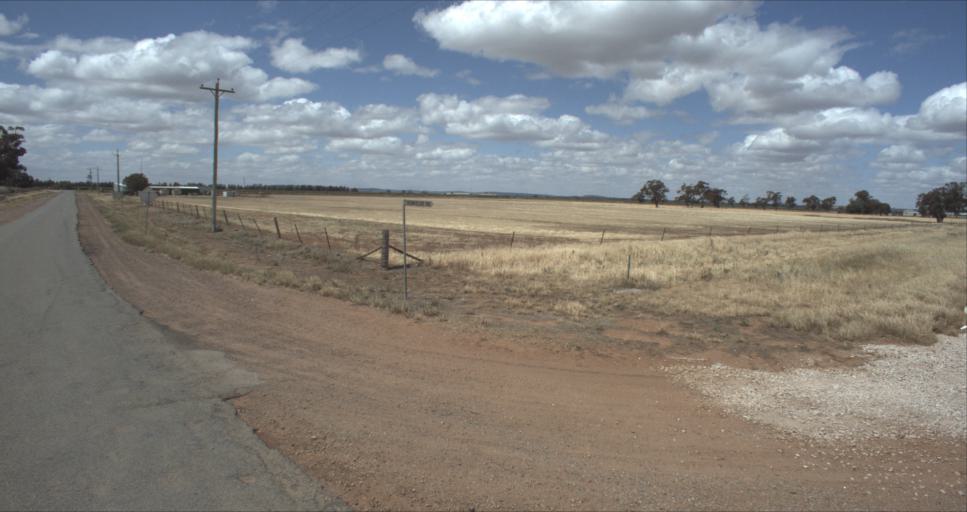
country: AU
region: New South Wales
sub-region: Leeton
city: Leeton
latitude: -34.5900
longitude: 146.3696
